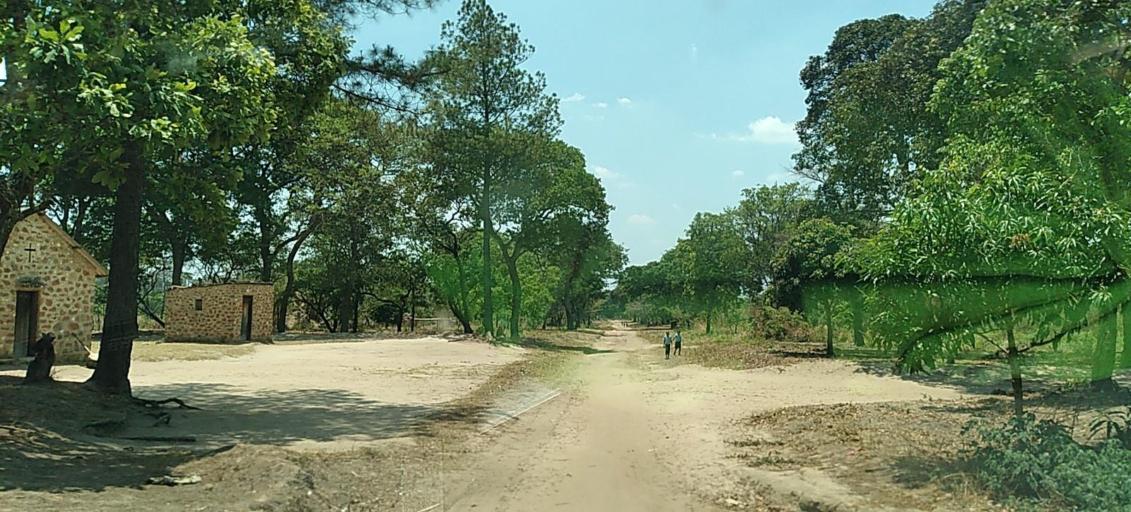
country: CD
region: Katanga
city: Kolwezi
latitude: -11.3771
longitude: 25.2165
